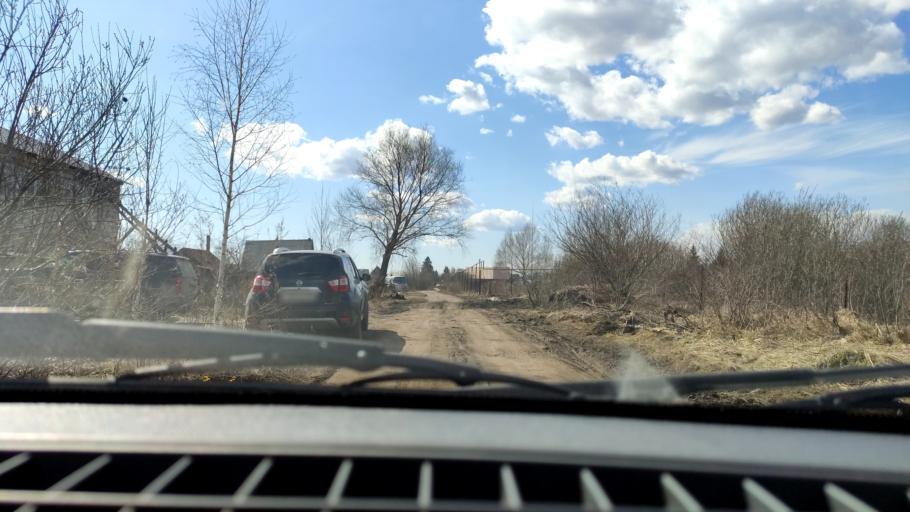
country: RU
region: Bashkortostan
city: Avdon
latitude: 54.6815
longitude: 55.8188
